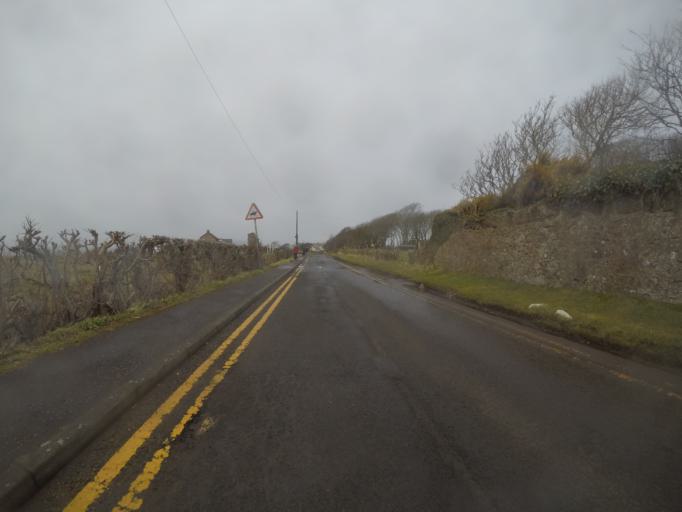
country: GB
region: Scotland
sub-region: North Ayrshire
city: West Kilbride
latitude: 55.6978
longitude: -4.9017
